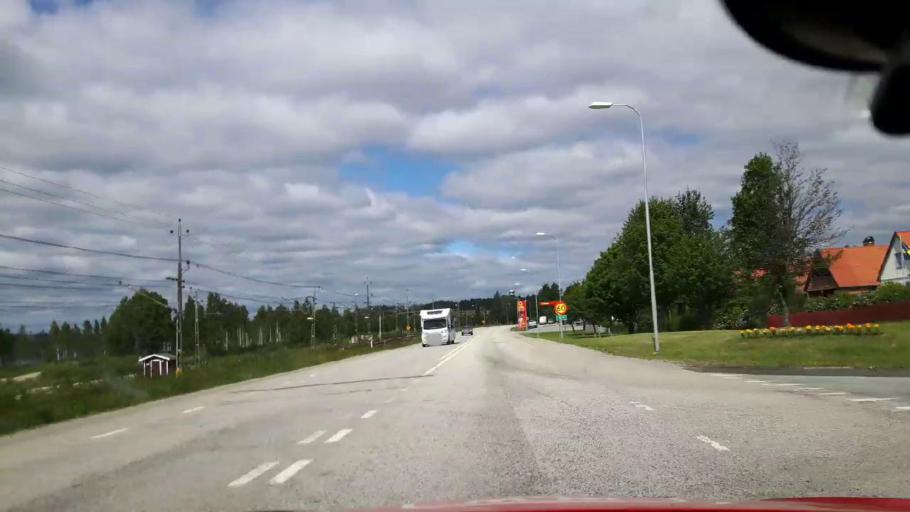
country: SE
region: Jaemtland
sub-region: Braecke Kommun
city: Braecke
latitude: 62.7462
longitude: 15.4223
